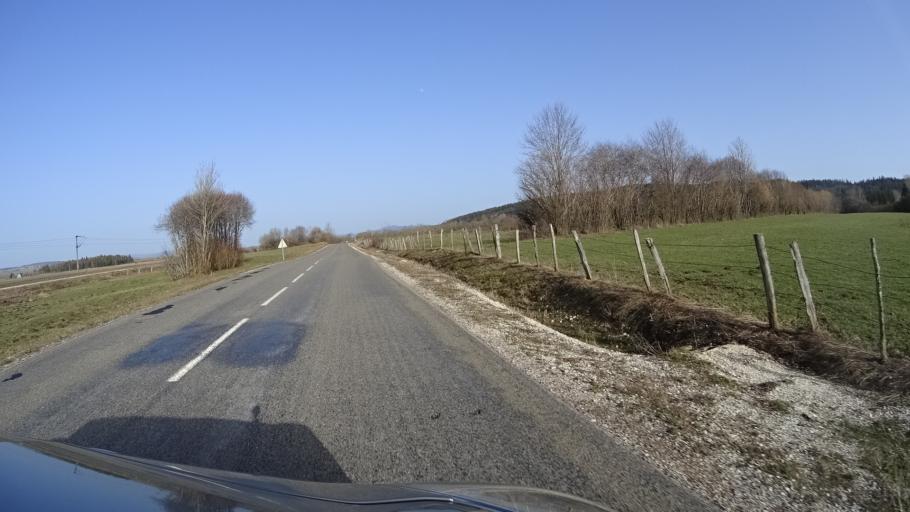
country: FR
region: Franche-Comte
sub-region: Departement du Doubs
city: Frasne
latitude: 46.8680
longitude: 6.2427
